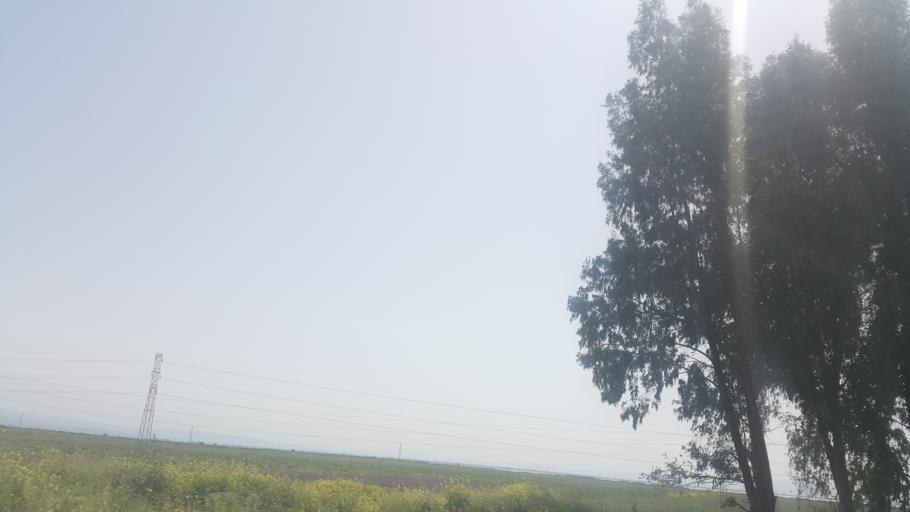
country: TR
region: Hatay
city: Serinyol
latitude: 36.4275
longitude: 36.2775
